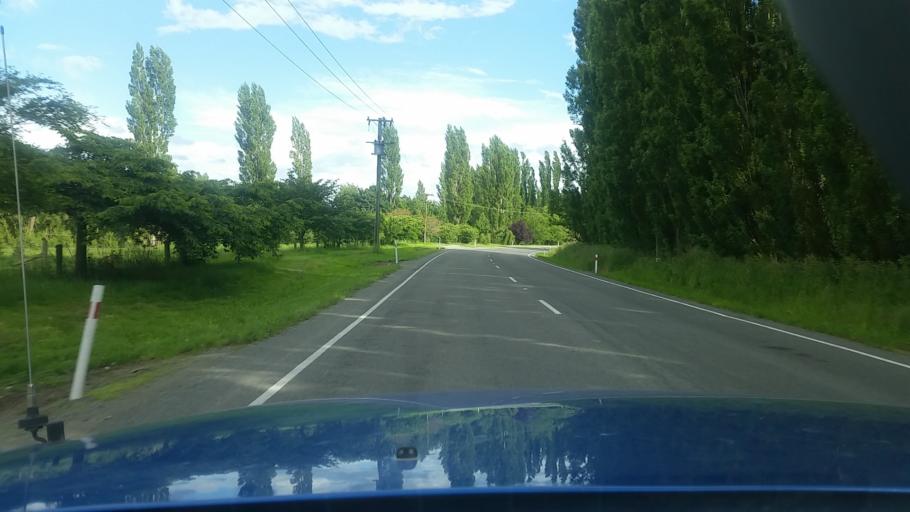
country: NZ
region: Canterbury
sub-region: Ashburton District
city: Ashburton
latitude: -43.8770
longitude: 171.7288
